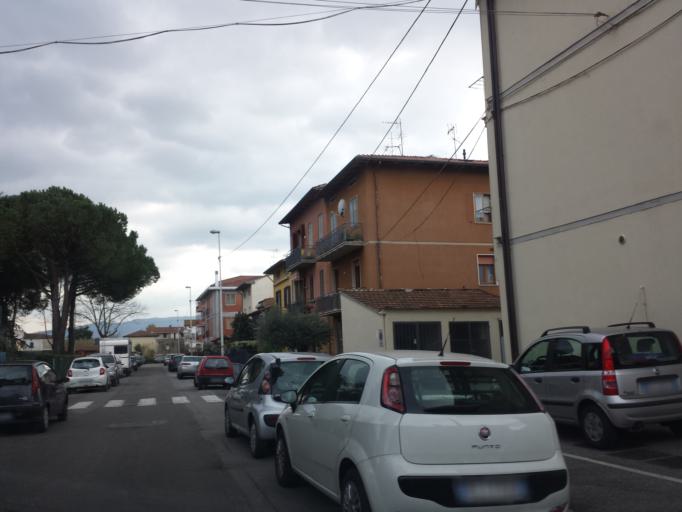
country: IT
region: Tuscany
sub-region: Provincia di Prato
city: Prato
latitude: 43.8871
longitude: 11.0597
